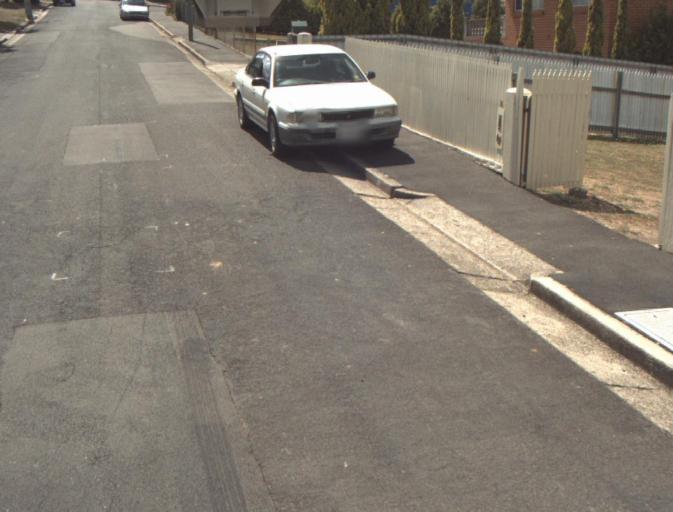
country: AU
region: Tasmania
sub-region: Launceston
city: Newnham
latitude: -41.4129
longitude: 147.1491
